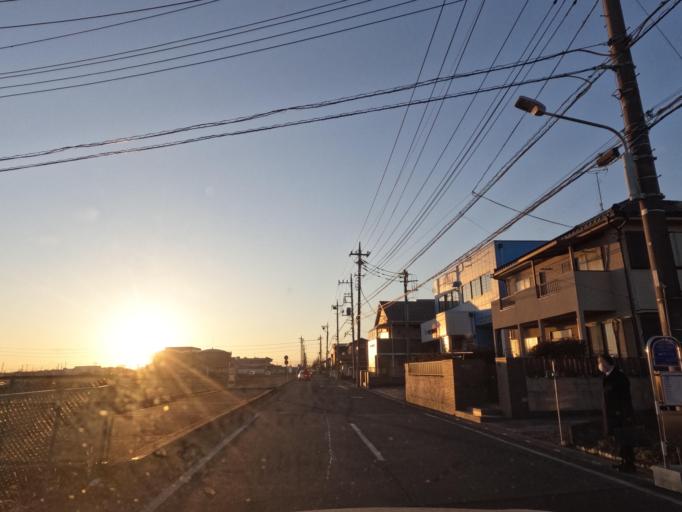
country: JP
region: Saitama
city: Kasukabe
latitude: 35.9633
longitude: 139.7538
